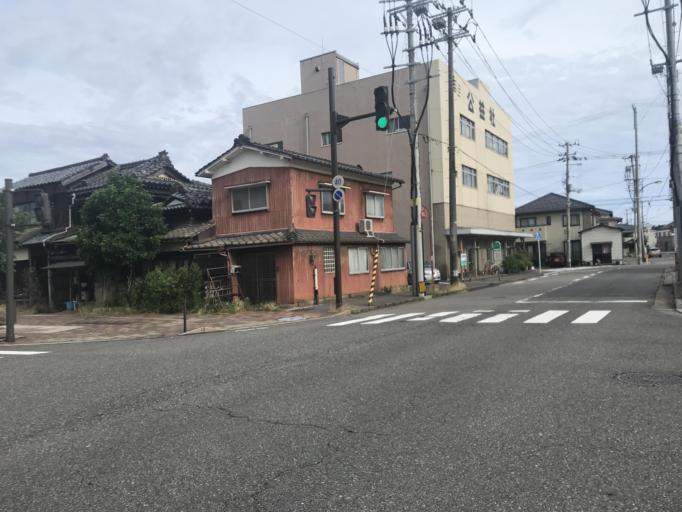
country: JP
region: Niigata
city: Niigata-shi
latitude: 37.9298
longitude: 139.0520
